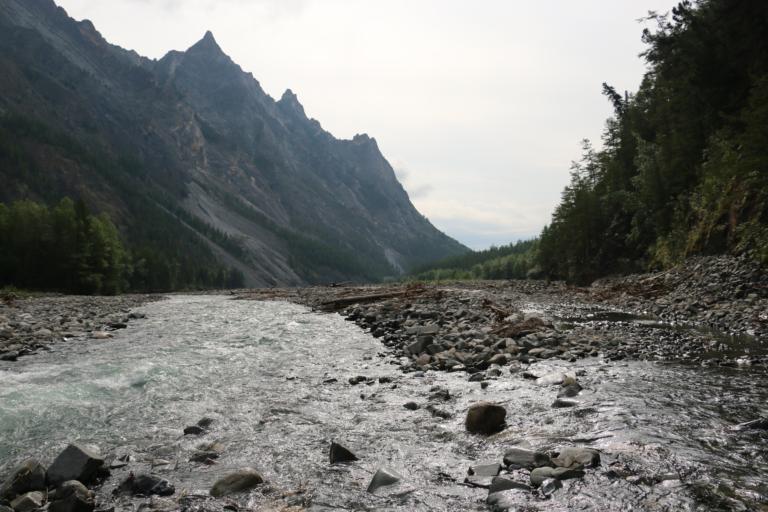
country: RU
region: Respublika Buryatiya
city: Novyy Uoyan
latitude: 56.2655
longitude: 111.4569
